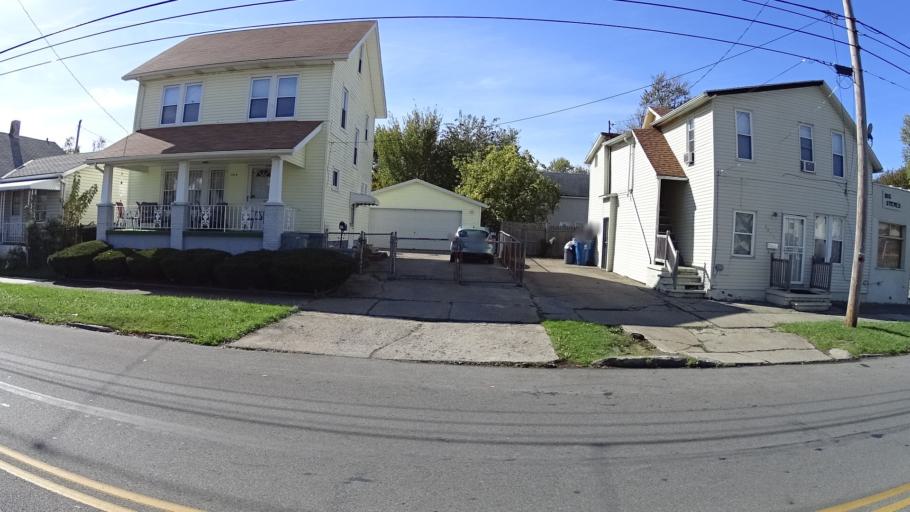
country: US
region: Ohio
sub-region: Lorain County
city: Lorain
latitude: 41.4576
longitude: -82.1704
